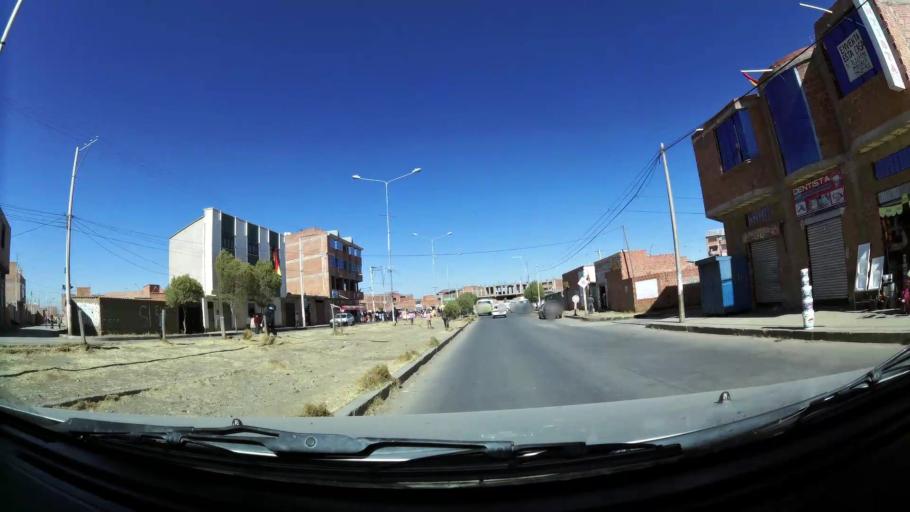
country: BO
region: La Paz
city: La Paz
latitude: -16.5276
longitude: -68.2203
